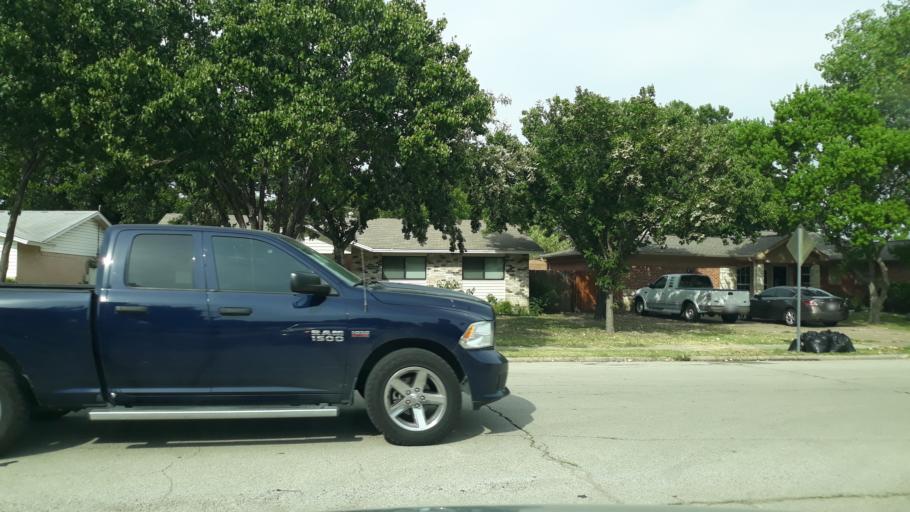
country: US
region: Texas
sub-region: Dallas County
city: Irving
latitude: 32.8456
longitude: -96.9874
